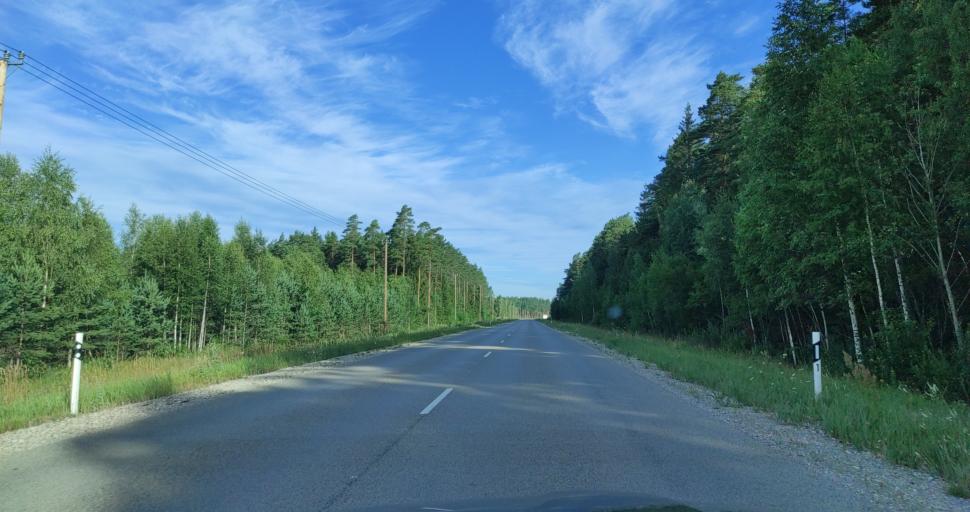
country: LV
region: Pavilostas
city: Pavilosta
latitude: 56.7922
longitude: 21.2428
